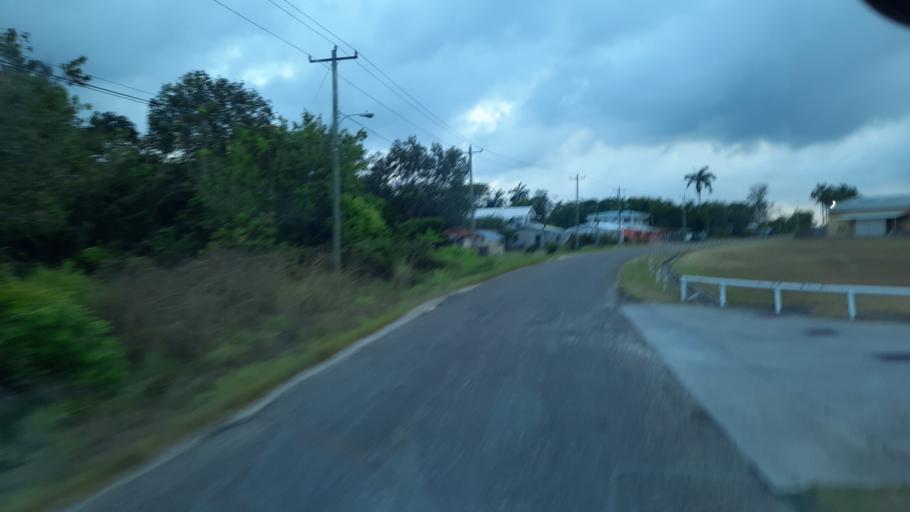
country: BZ
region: Belize
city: Belize City
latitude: 17.5450
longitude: -88.2967
